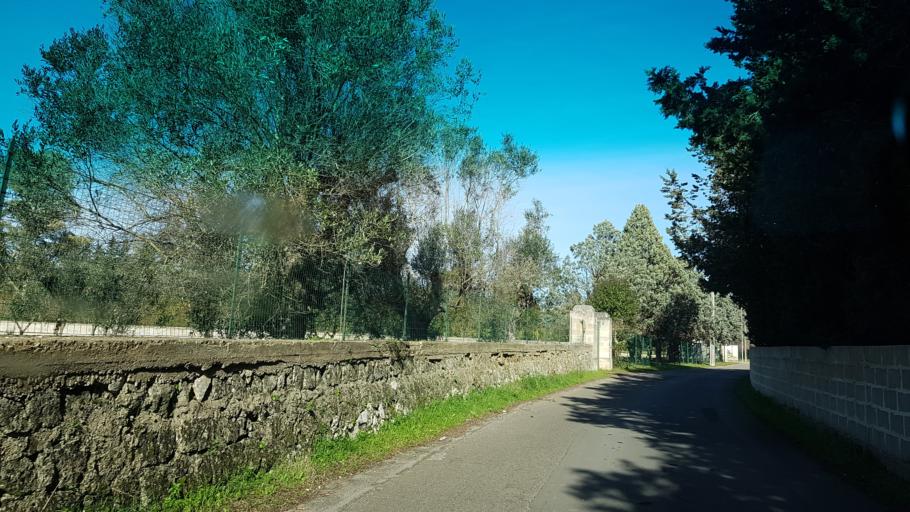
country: IT
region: Apulia
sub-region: Provincia di Lecce
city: Arnesano
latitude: 40.3572
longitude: 18.1052
